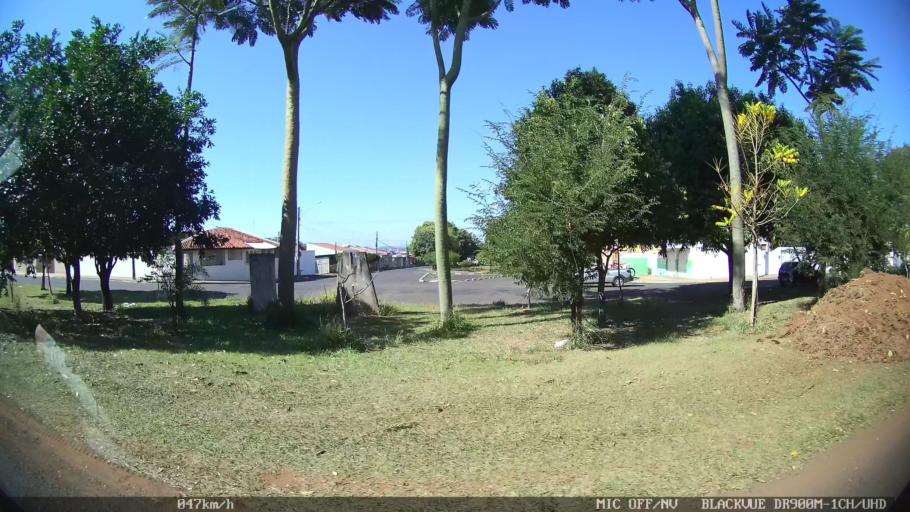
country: BR
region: Sao Paulo
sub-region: Batatais
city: Batatais
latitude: -20.8779
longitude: -47.5969
